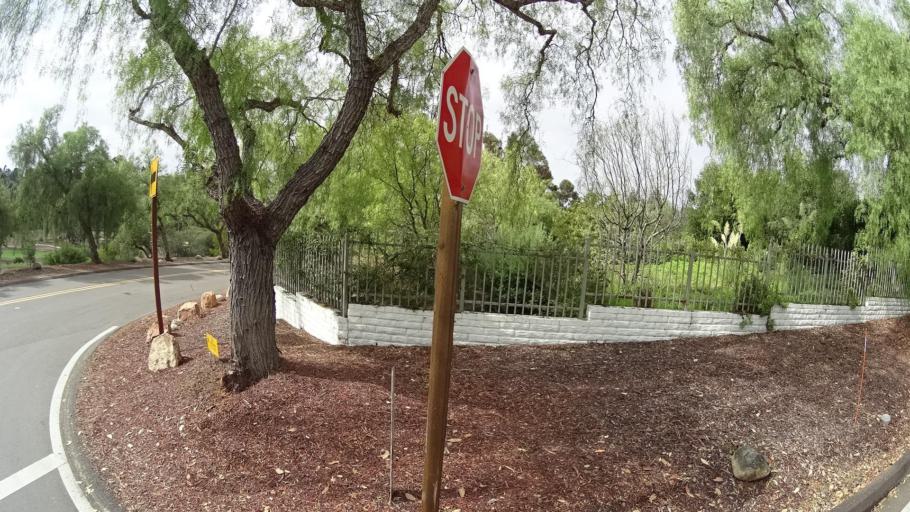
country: US
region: California
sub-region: San Diego County
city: Rancho Santa Fe
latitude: 33.0247
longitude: -117.2248
